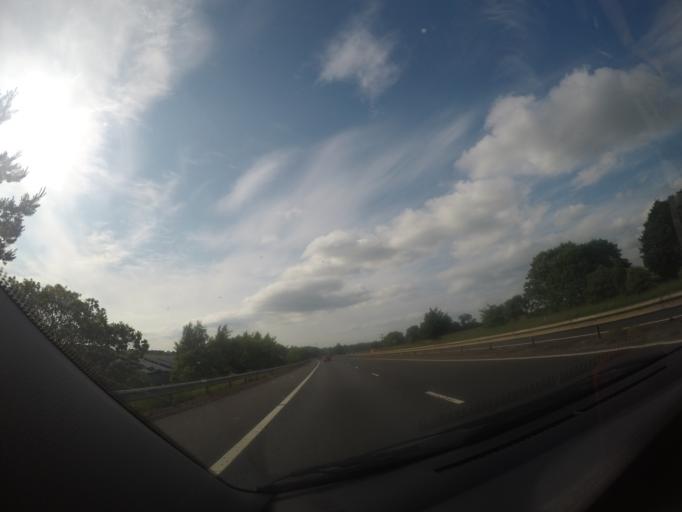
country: GB
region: Scotland
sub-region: South Lanarkshire
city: Lesmahagow
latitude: 55.6421
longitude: -3.8793
